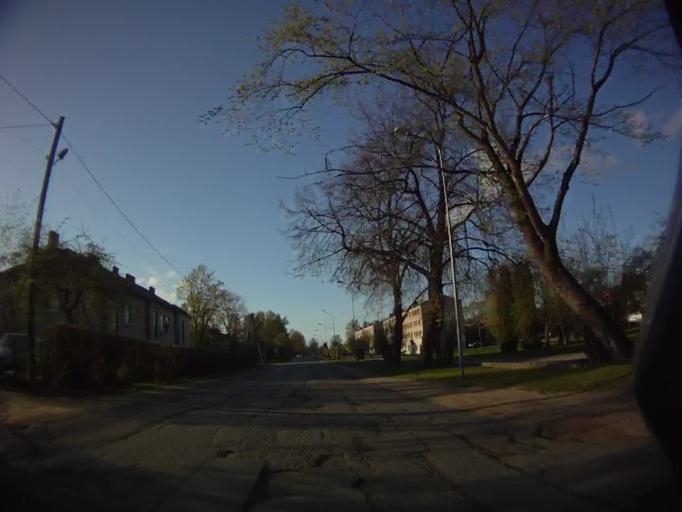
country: LV
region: Sigulda
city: Sigulda
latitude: 57.1485
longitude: 24.8916
